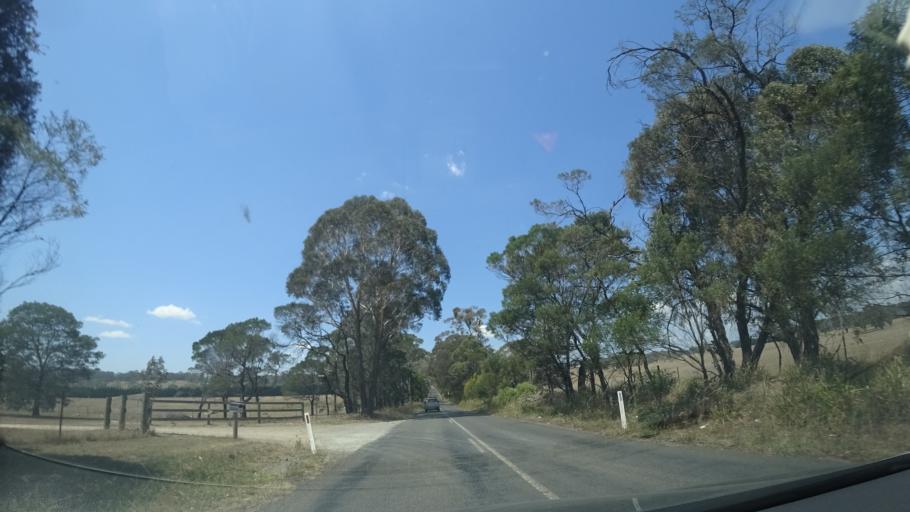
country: AU
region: New South Wales
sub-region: Wingecarribee
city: Bundanoon
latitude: -34.6099
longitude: 150.2332
